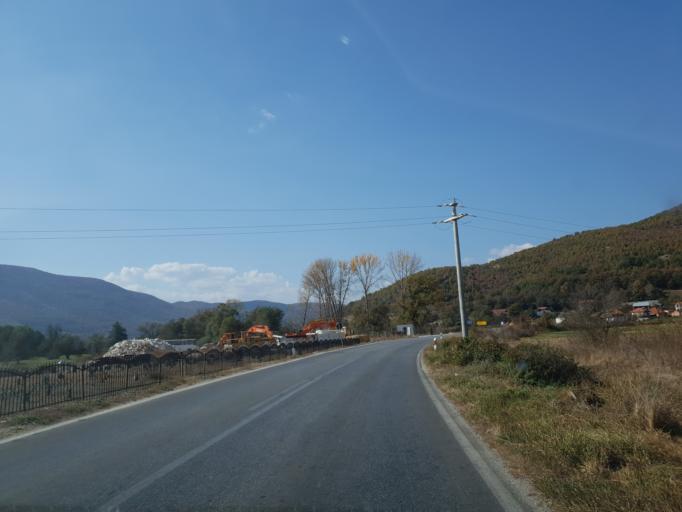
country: MK
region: Plasnica
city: Lisicani
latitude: 41.4687
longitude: 21.0318
